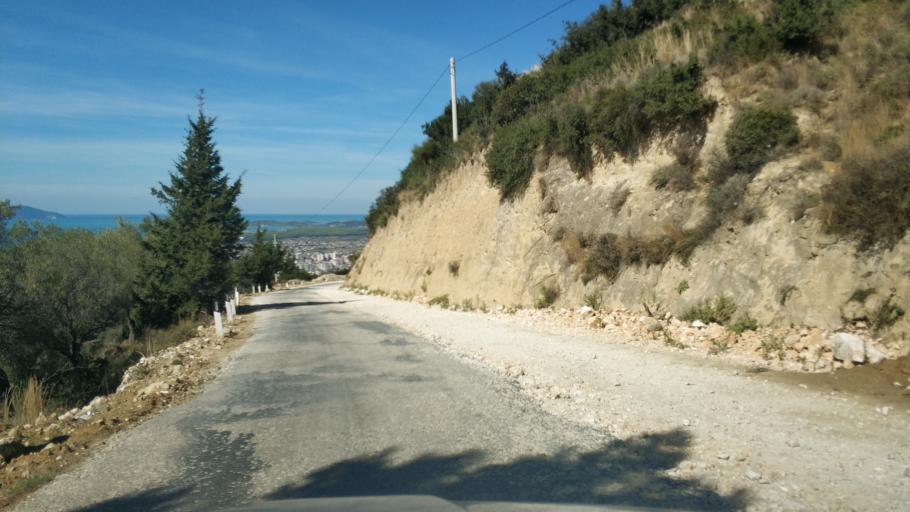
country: AL
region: Vlore
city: Vlore
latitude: 40.4478
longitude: 19.5172
